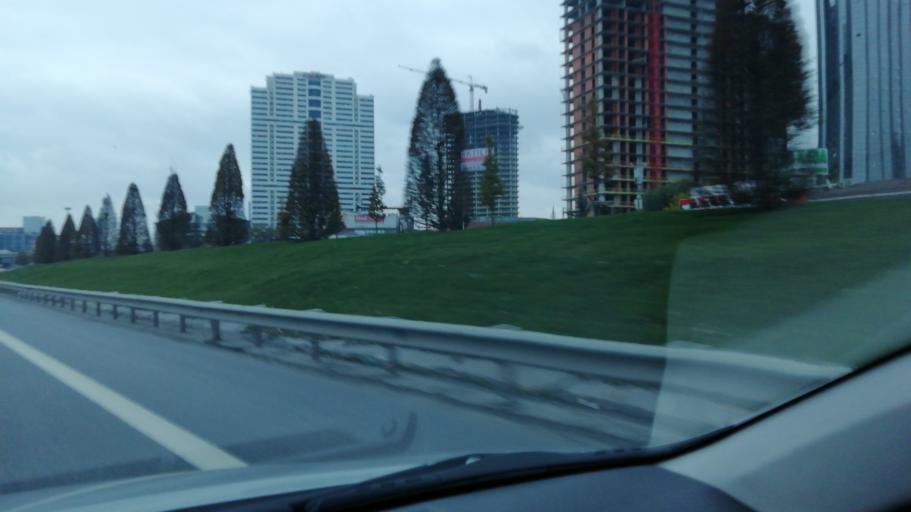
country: TR
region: Istanbul
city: Mahmutbey
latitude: 41.0427
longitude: 28.8090
